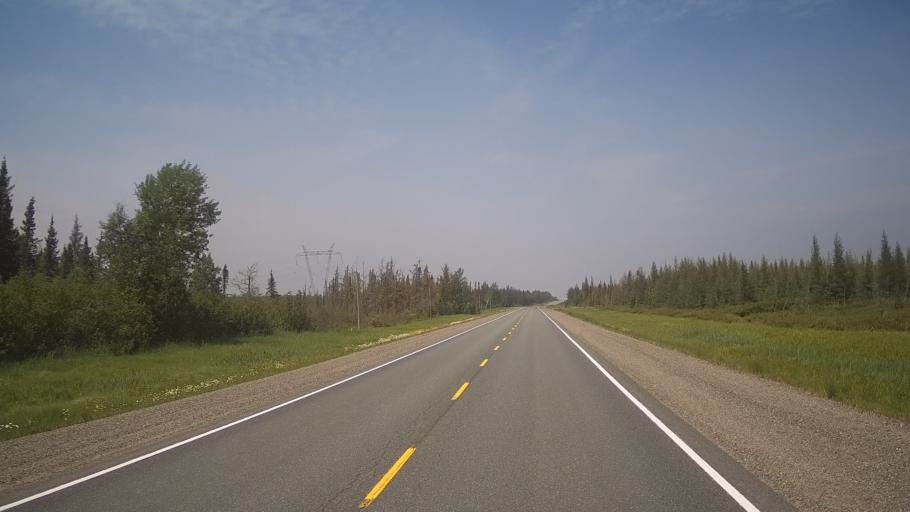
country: CA
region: Ontario
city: Timmins
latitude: 48.7624
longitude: -81.3612
